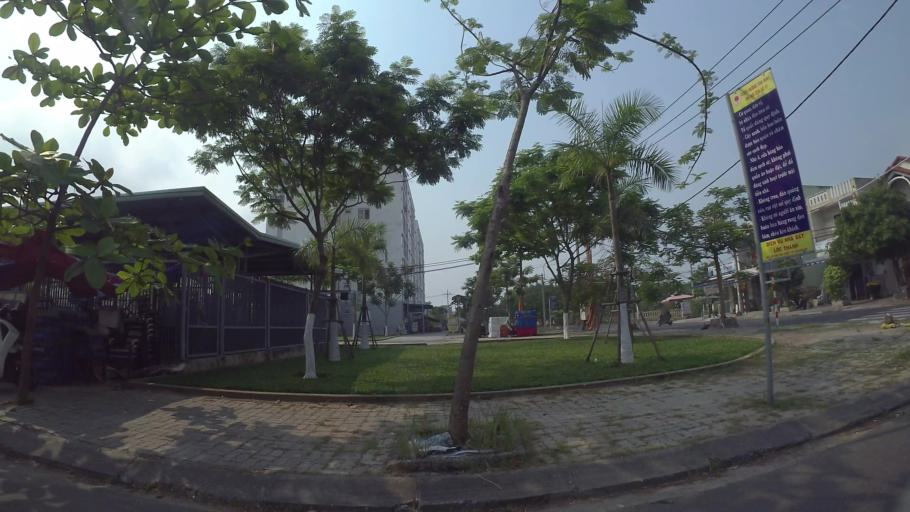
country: VN
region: Da Nang
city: Cam Le
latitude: 15.9993
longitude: 108.2134
